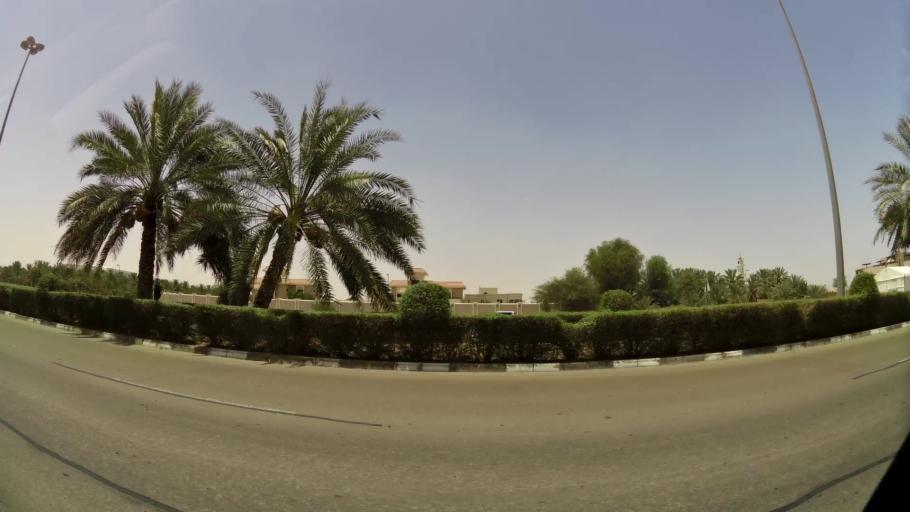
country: OM
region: Al Buraimi
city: Al Buraymi
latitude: 24.2591
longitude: 55.7170
